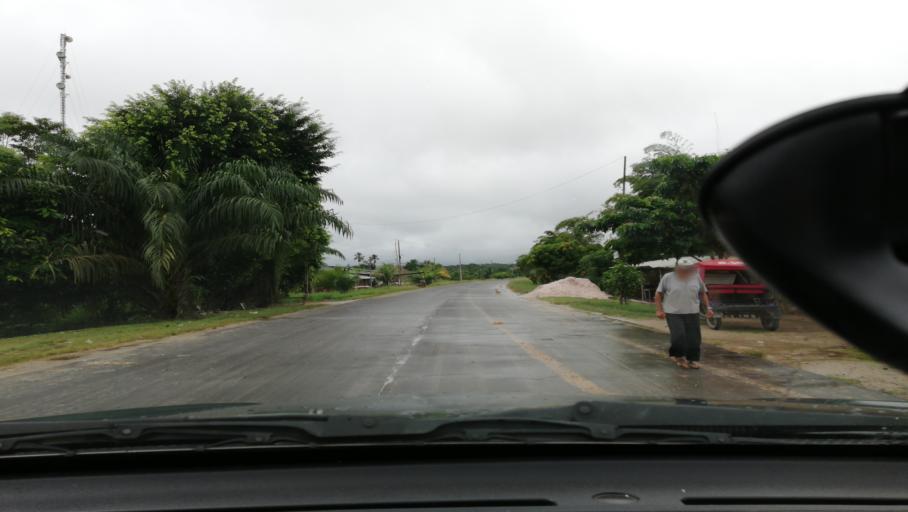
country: PE
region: Loreto
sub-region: Provincia de Loreto
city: Nauta
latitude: -4.2311
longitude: -73.4865
